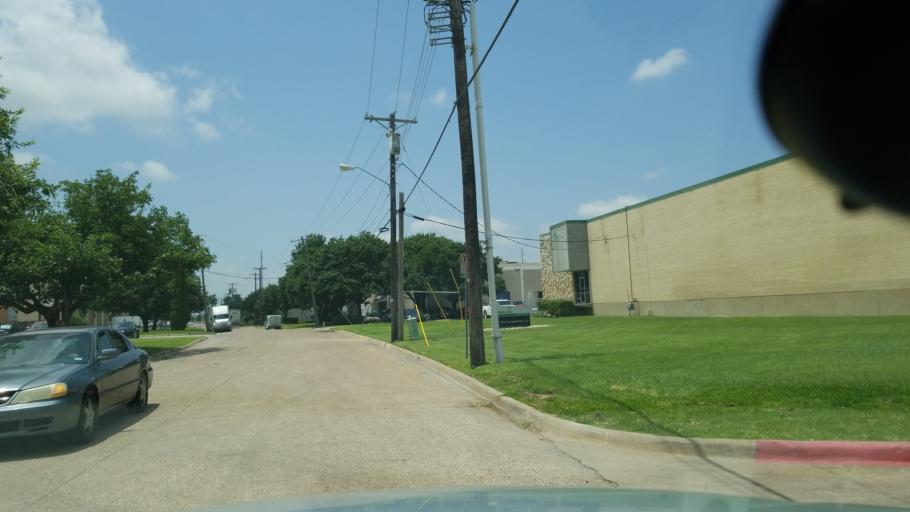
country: US
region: Texas
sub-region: Dallas County
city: Irving
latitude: 32.8283
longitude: -96.8777
